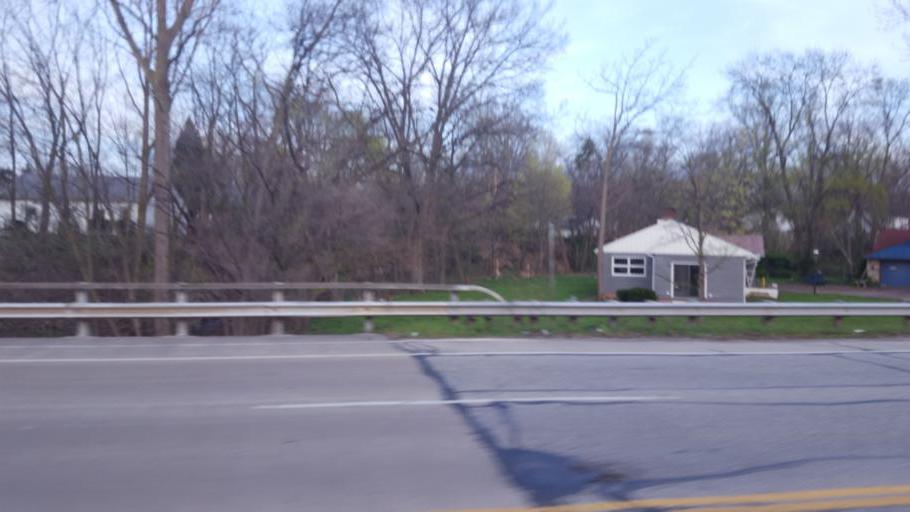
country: US
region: Ohio
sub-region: Lorain County
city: Amherst
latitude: 41.4222
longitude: -82.2088
